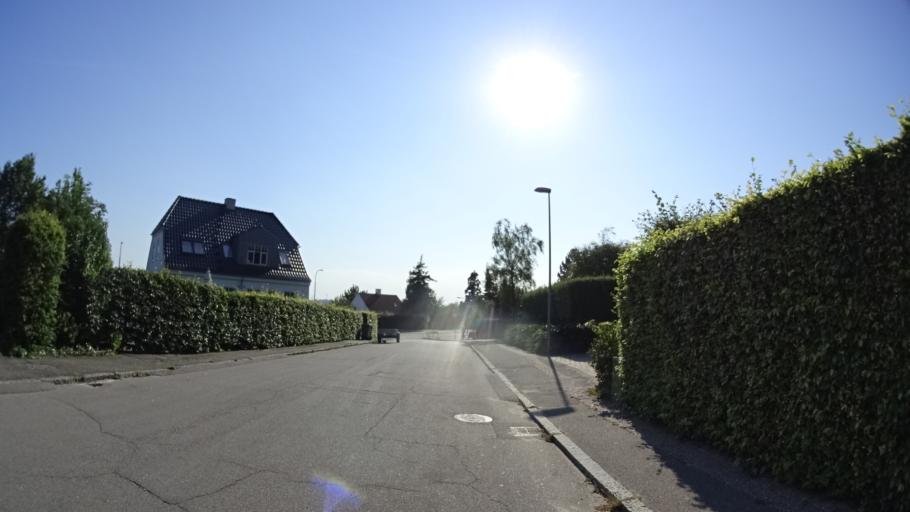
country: DK
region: Central Jutland
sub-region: Arhus Kommune
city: Stavtrup
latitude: 56.1549
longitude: 10.1089
